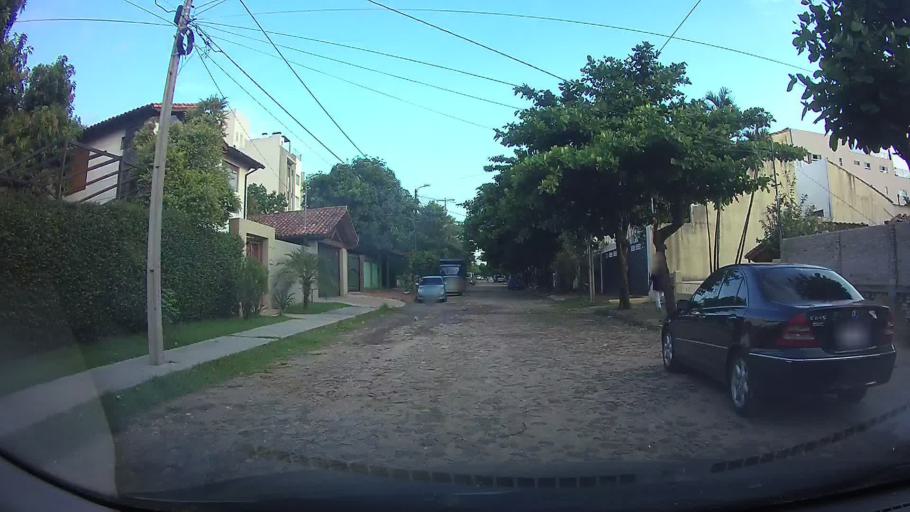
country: PY
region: Asuncion
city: Asuncion
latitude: -25.2665
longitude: -57.5745
